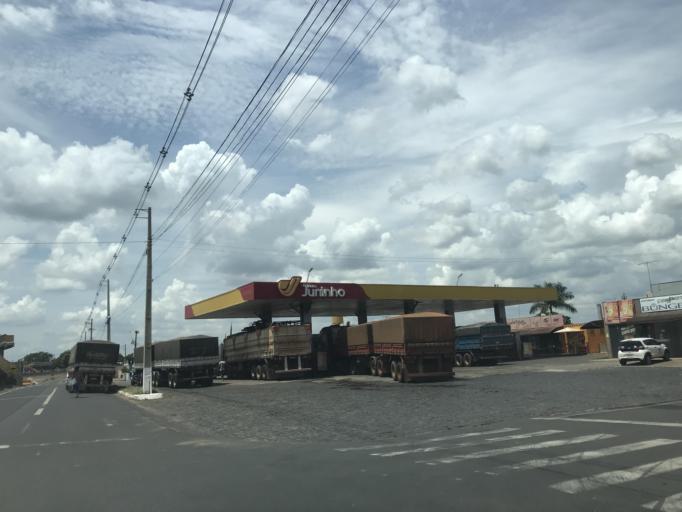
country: BR
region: Parana
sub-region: Mandaguacu
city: Mandaguacu
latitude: -23.2763
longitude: -52.1549
